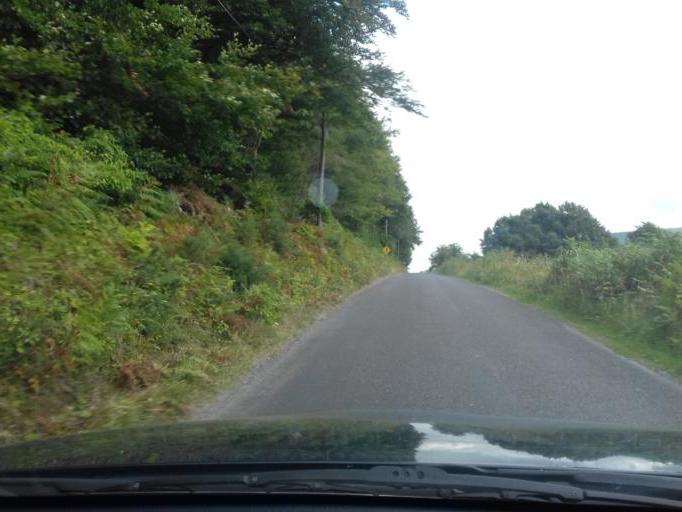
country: IE
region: Leinster
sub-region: Loch Garman
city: Bunclody
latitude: 52.6452
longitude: -6.7222
